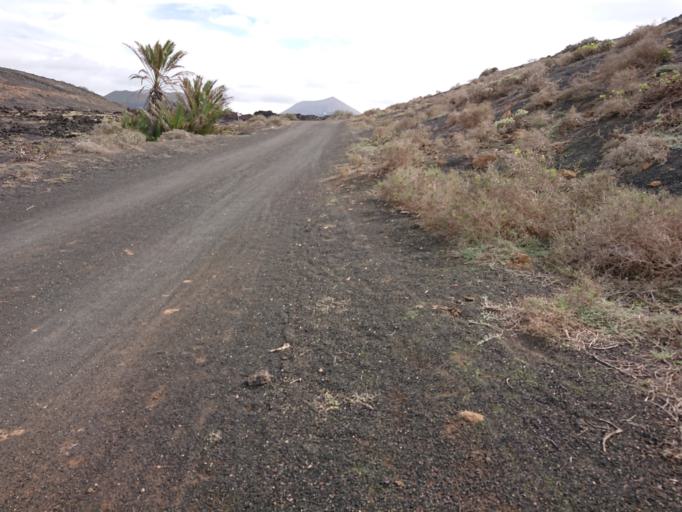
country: ES
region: Canary Islands
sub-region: Provincia de Las Palmas
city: Tinajo
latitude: 29.0190
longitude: -13.6758
